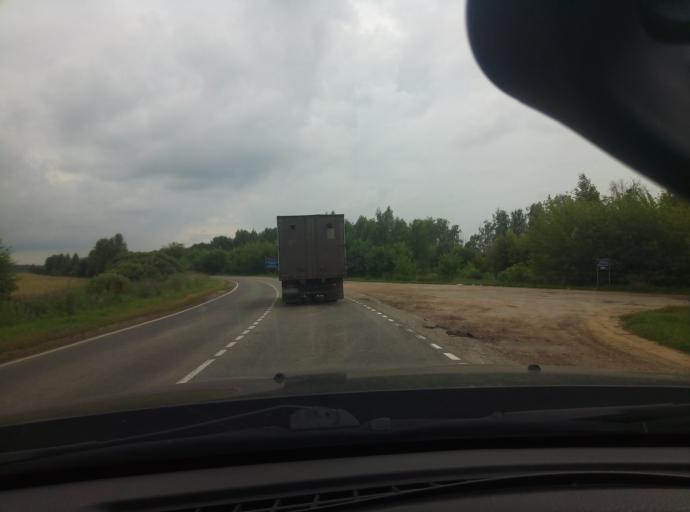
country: RU
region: Tula
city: Kimovsk
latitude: 53.9494
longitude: 38.5327
